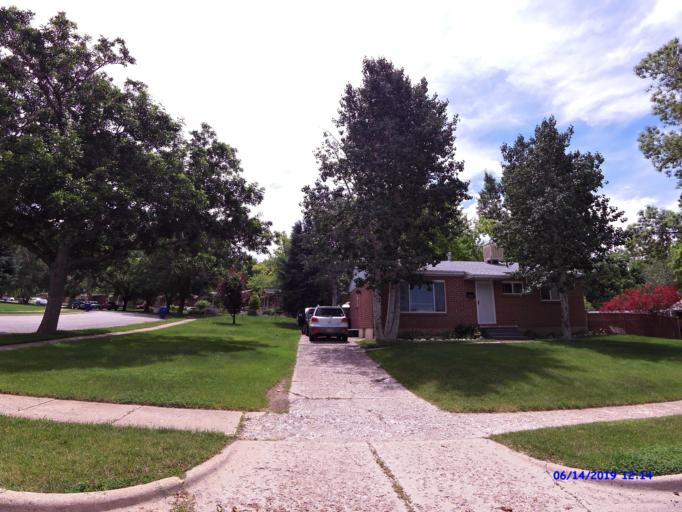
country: US
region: Utah
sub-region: Weber County
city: Ogden
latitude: 41.2570
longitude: -111.9504
